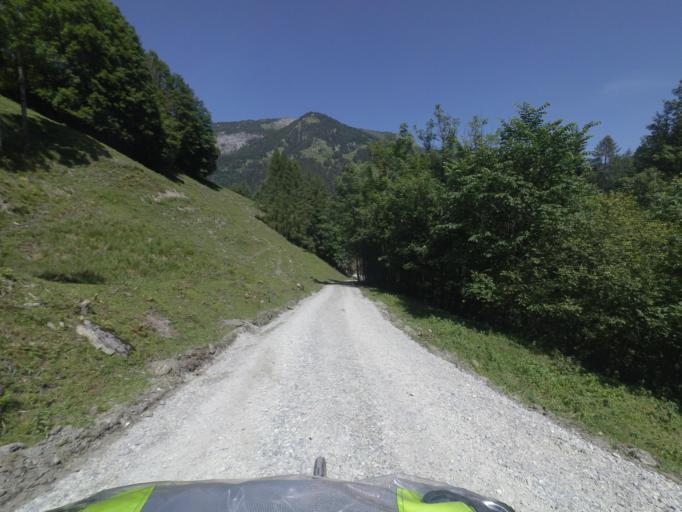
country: AT
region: Salzburg
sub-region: Politischer Bezirk Sankt Johann im Pongau
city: Dorfgastein
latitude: 47.2581
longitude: 13.0756
